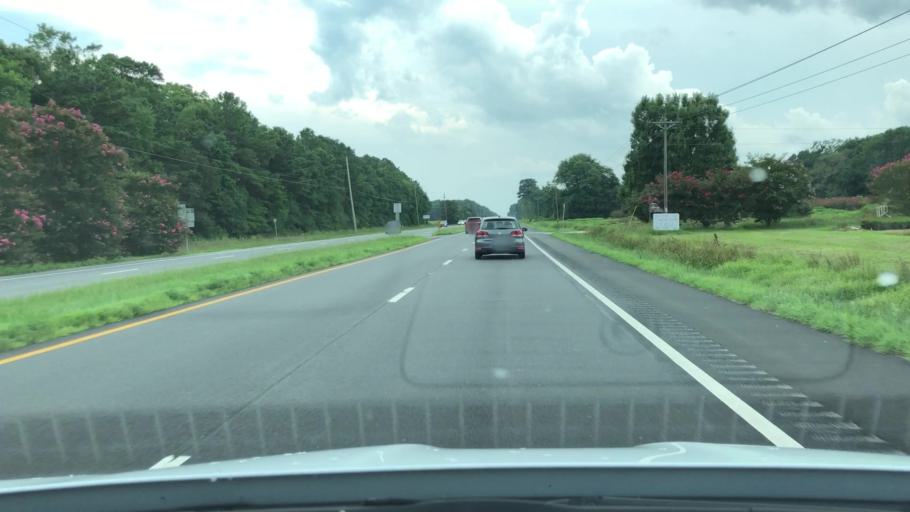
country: US
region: Virginia
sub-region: Northampton County
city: Exmore
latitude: 37.5120
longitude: -75.8340
